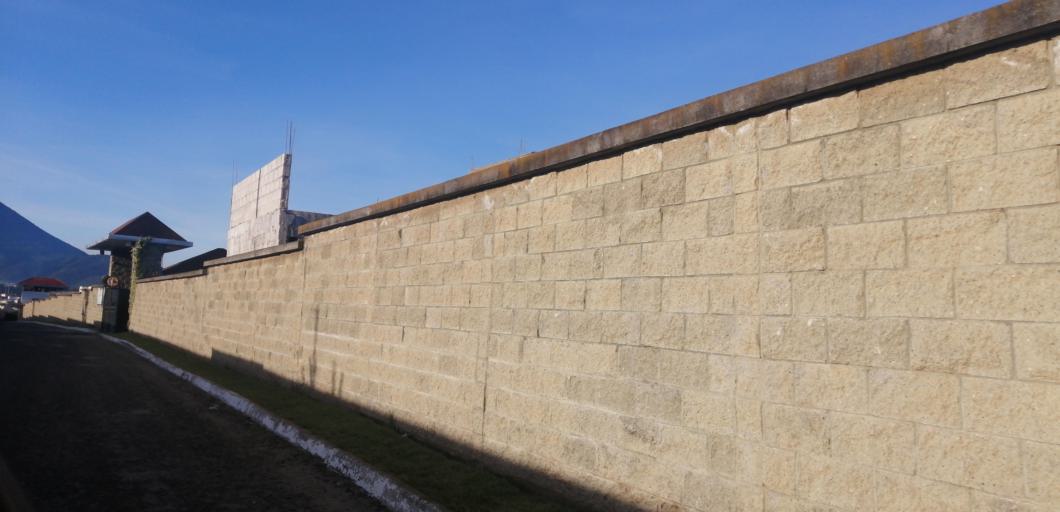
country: GT
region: Quetzaltenango
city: Olintepeque
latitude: 14.8665
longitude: -91.5332
